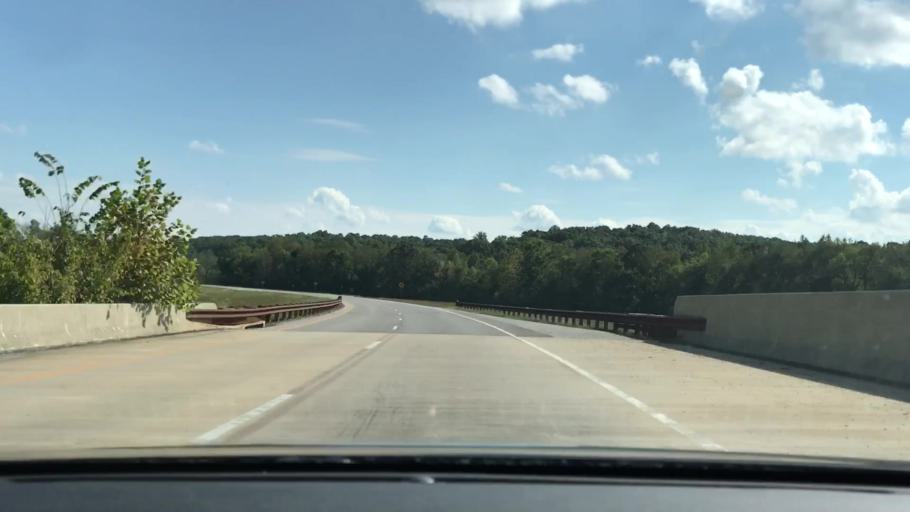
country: US
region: Kentucky
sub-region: Trigg County
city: Cadiz
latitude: 36.7846
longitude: -88.0215
